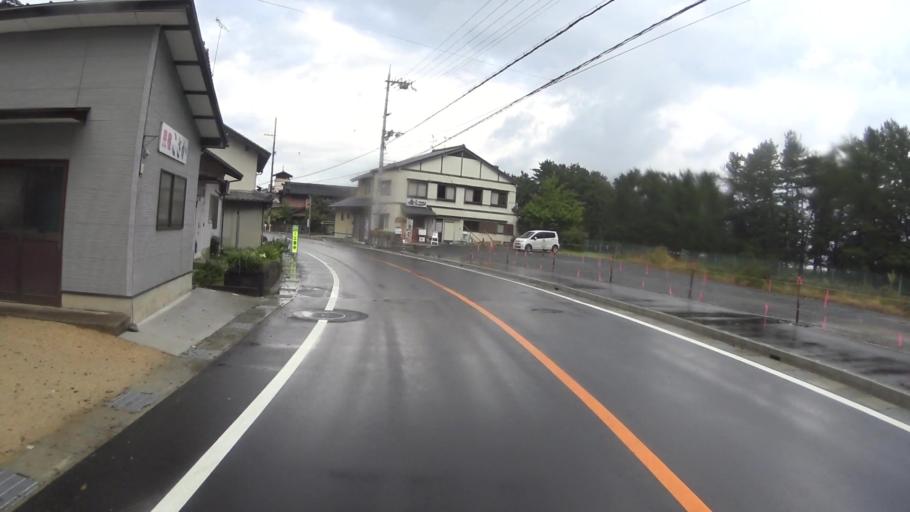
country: JP
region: Kyoto
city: Miyazu
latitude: 35.5541
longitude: 135.1858
